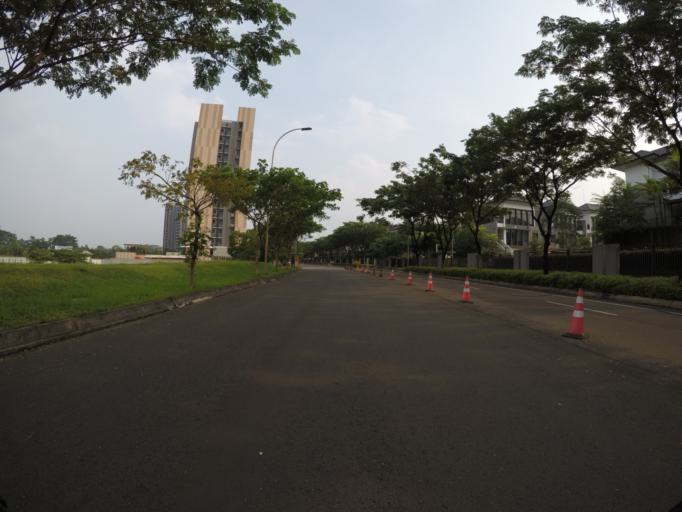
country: ID
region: West Java
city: Serpong
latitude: -6.2946
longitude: 106.6504
